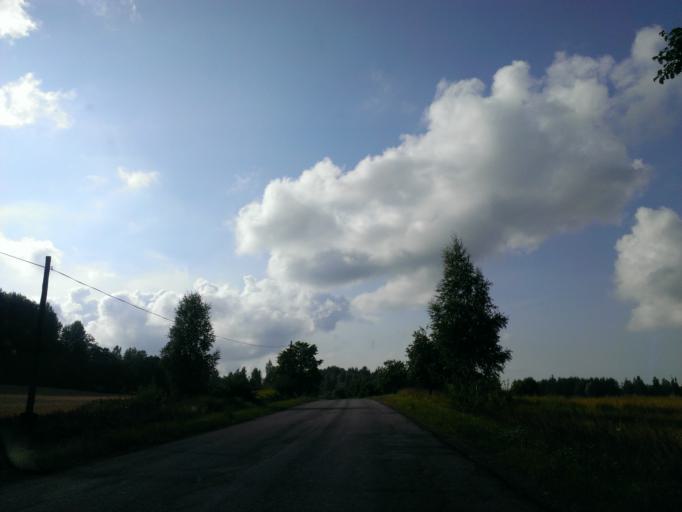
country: LV
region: Priekuli
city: Priekuli
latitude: 57.3136
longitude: 25.3779
